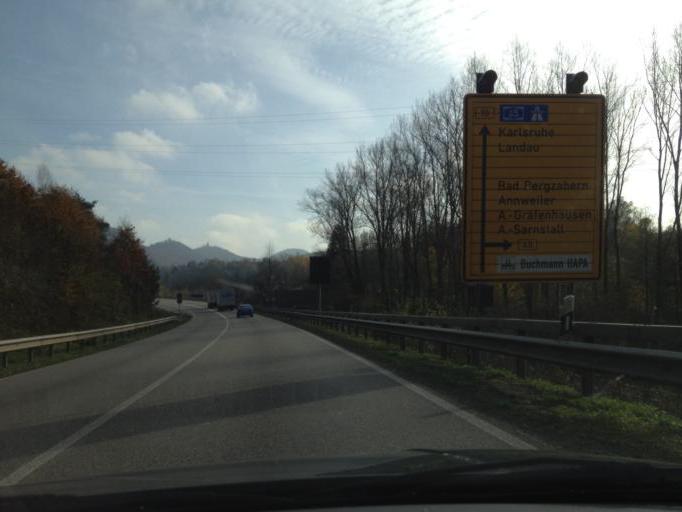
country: DE
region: Rheinland-Pfalz
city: Wernersberg
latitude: 49.2052
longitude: 7.9450
